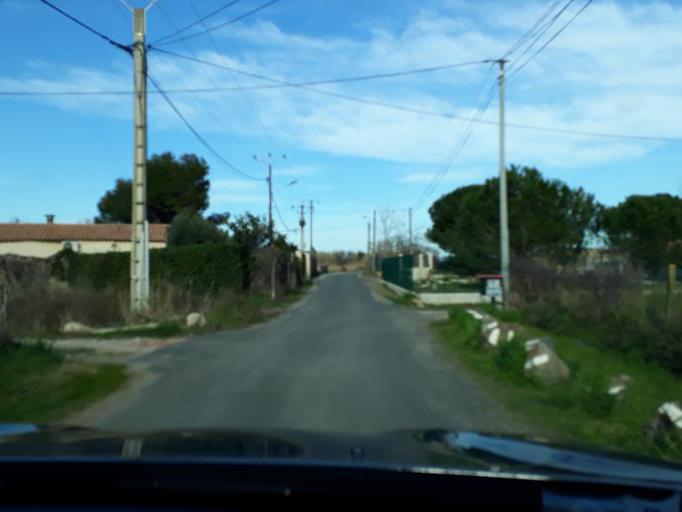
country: FR
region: Languedoc-Roussillon
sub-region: Departement de l'Herault
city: Marseillan
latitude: 43.3314
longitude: 3.5528
